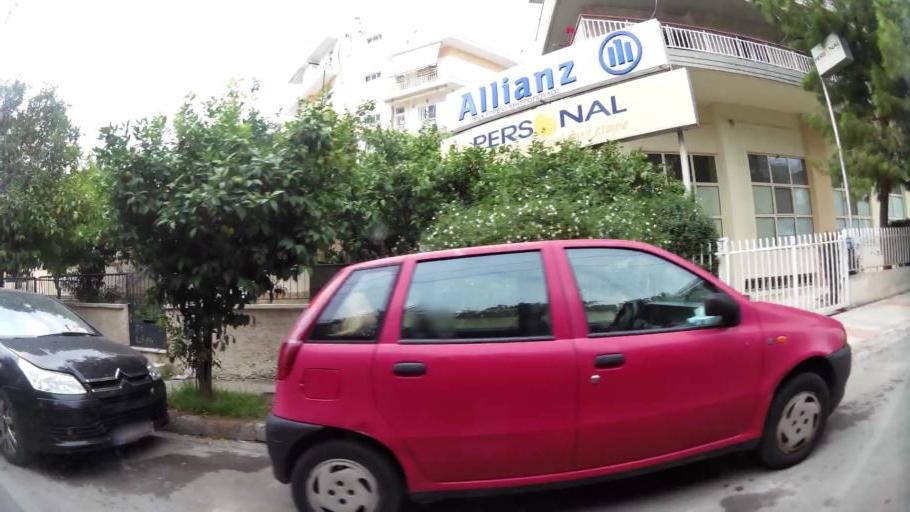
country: GR
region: Attica
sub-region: Nomarchia Athinas
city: Ilion
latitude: 38.0347
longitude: 23.7082
